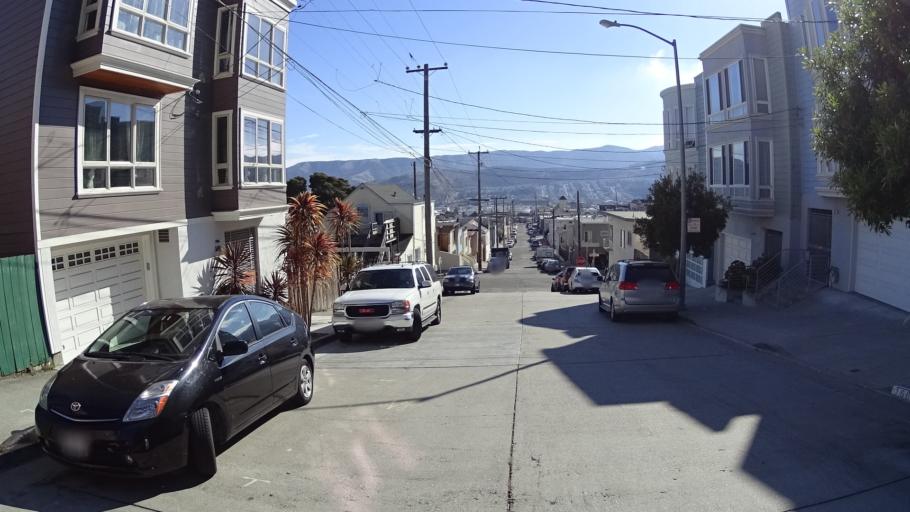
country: US
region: California
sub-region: San Mateo County
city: Brisbane
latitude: 37.7163
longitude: -122.4081
